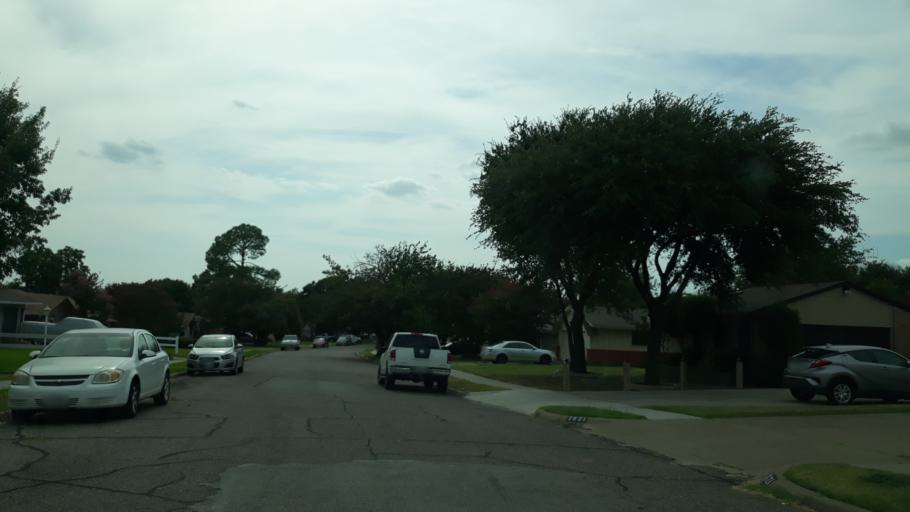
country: US
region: Texas
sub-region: Dallas County
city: Irving
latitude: 32.8515
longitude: -96.9843
